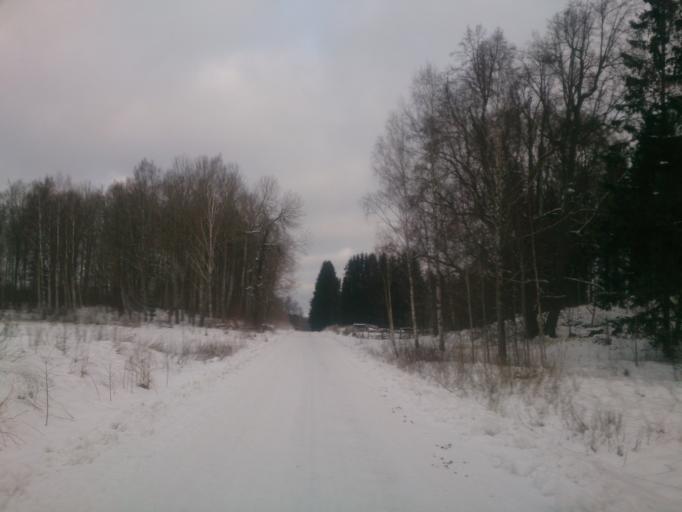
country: SE
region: OEstergoetland
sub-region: Atvidabergs Kommun
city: Atvidaberg
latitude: 58.2177
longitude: 15.9897
